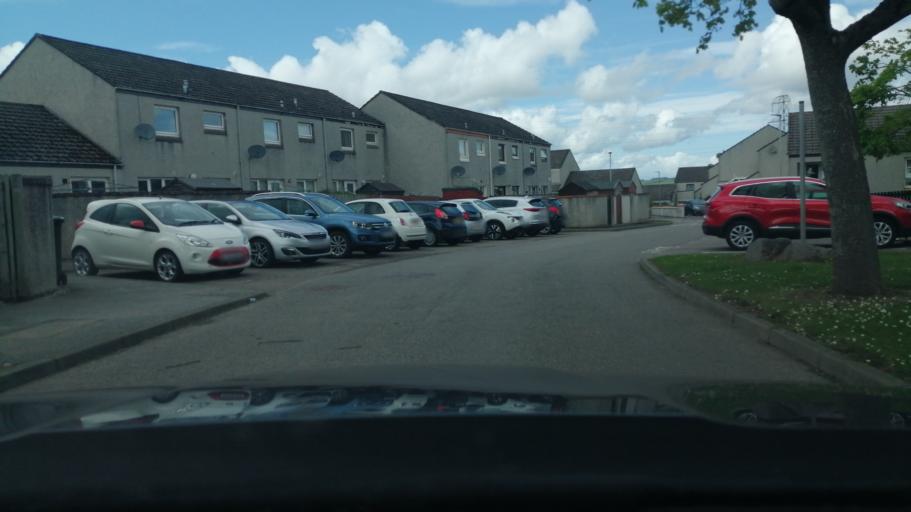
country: GB
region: Scotland
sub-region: Moray
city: Keith
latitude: 57.5351
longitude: -2.9427
